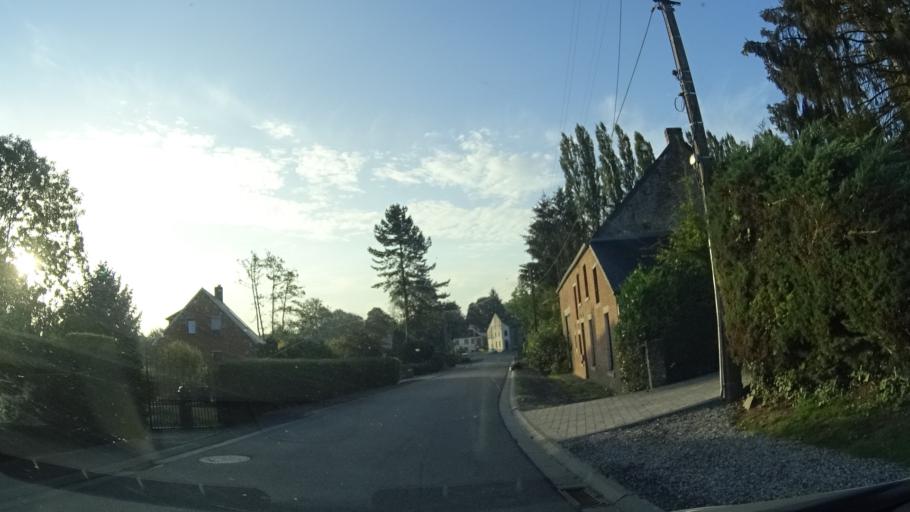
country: BE
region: Wallonia
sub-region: Province du Hainaut
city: Beaumont
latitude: 50.2603
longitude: 4.2347
